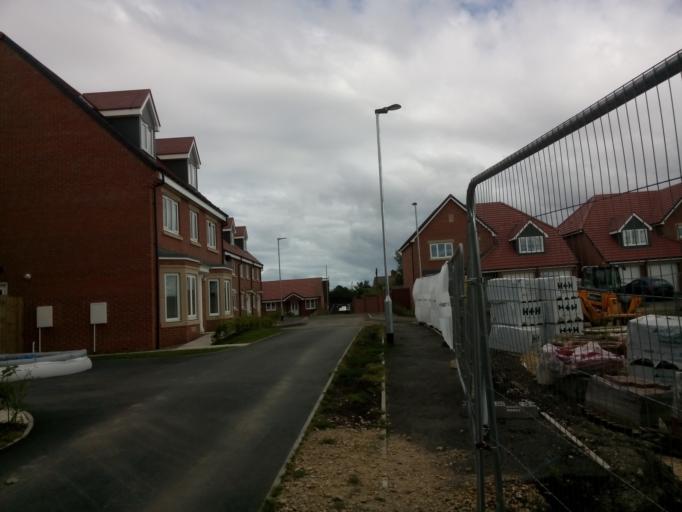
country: GB
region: England
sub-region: County Durham
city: Durham
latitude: 54.7998
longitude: -1.5826
